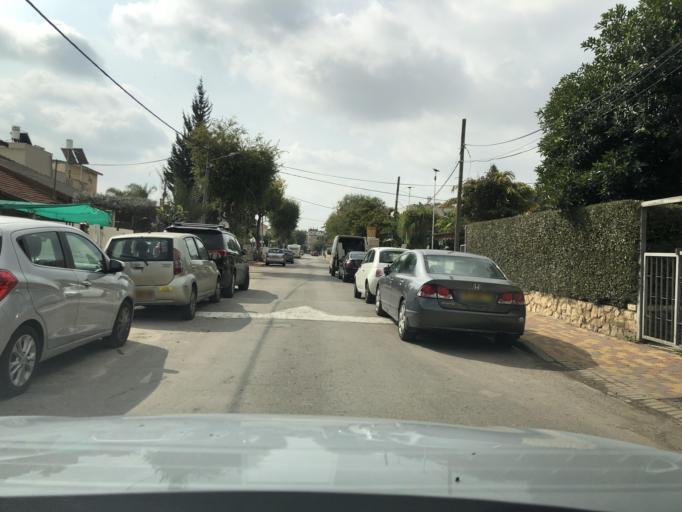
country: IL
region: Central District
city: Yehud
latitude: 32.0341
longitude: 34.8964
